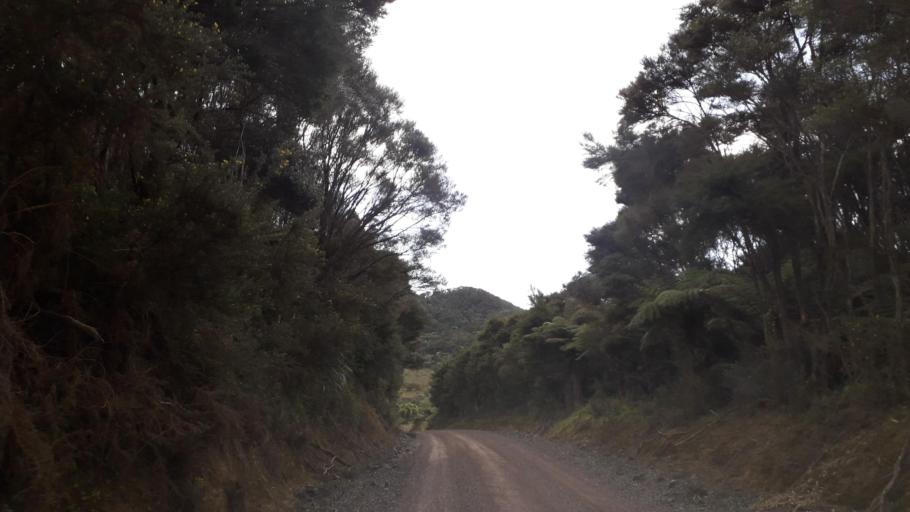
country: NZ
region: Northland
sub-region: Far North District
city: Paihia
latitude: -35.3306
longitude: 174.2321
